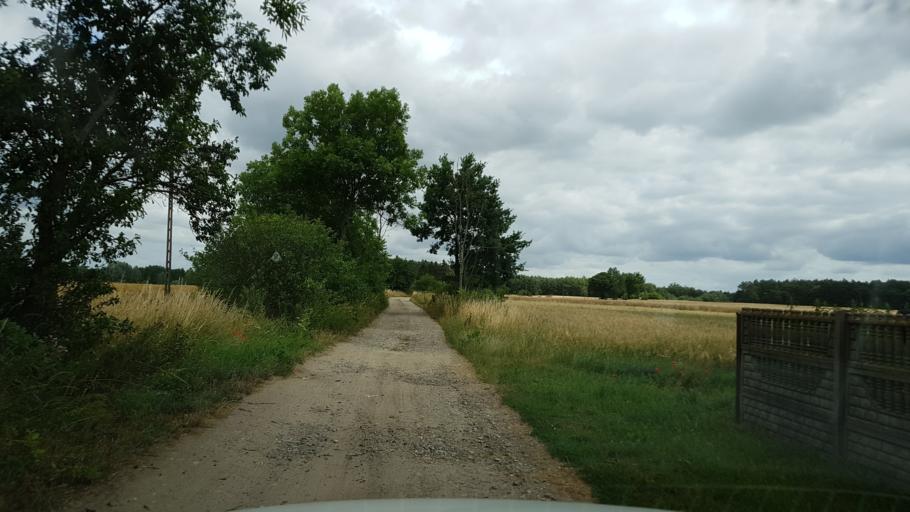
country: PL
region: West Pomeranian Voivodeship
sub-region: Powiat mysliborski
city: Mysliborz
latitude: 52.9393
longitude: 14.8991
